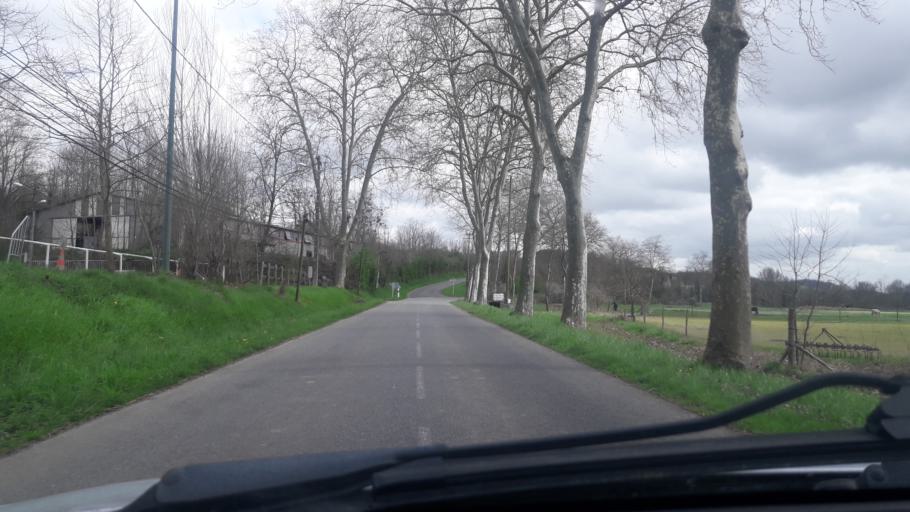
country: FR
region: Midi-Pyrenees
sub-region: Departement de la Haute-Garonne
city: Rieux-Volvestre
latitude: 43.2579
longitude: 1.2388
